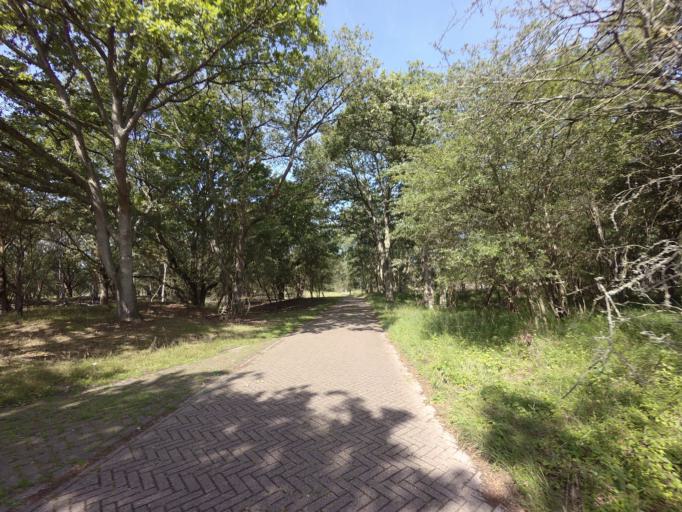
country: NL
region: South Holland
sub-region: Gemeente Leidschendam-Voorburg
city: Voorburg
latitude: 52.1313
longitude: 4.3425
